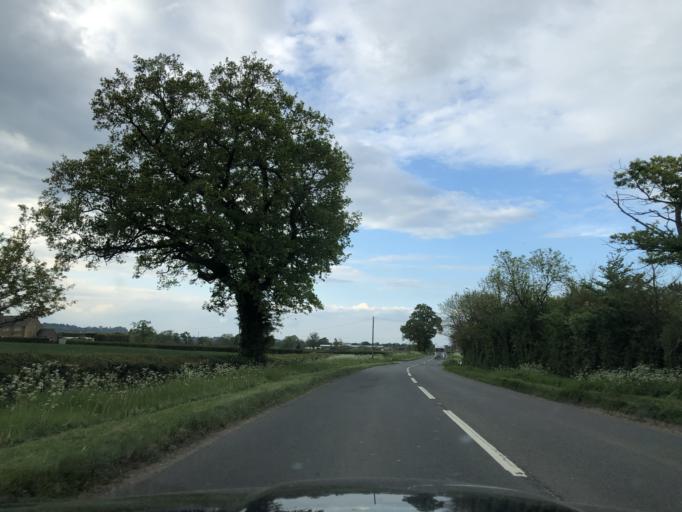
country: GB
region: England
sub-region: Gloucestershire
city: Moreton in Marsh
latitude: 51.9741
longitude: -1.7079
